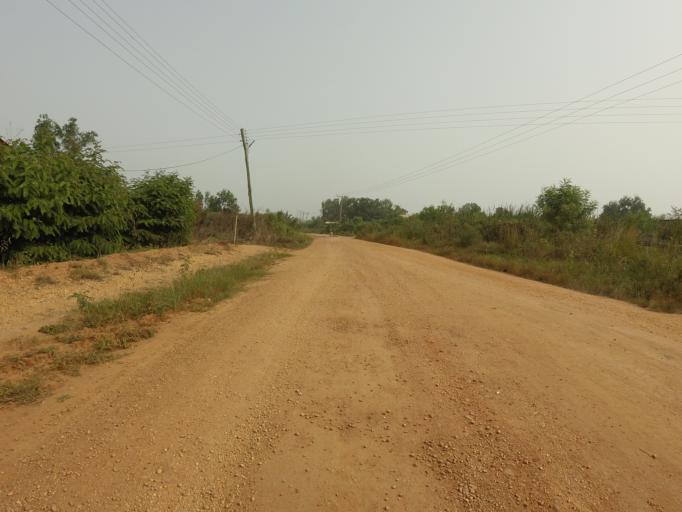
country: GH
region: Volta
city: Anloga
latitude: 5.9904
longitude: 0.5956
